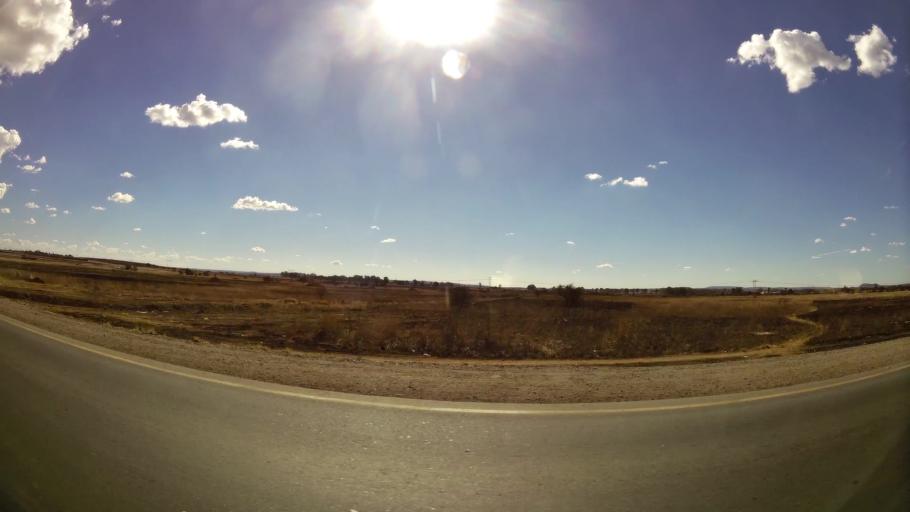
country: ZA
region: North-West
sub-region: Dr Kenneth Kaunda District Municipality
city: Klerksdorp
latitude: -26.8713
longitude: 26.6124
